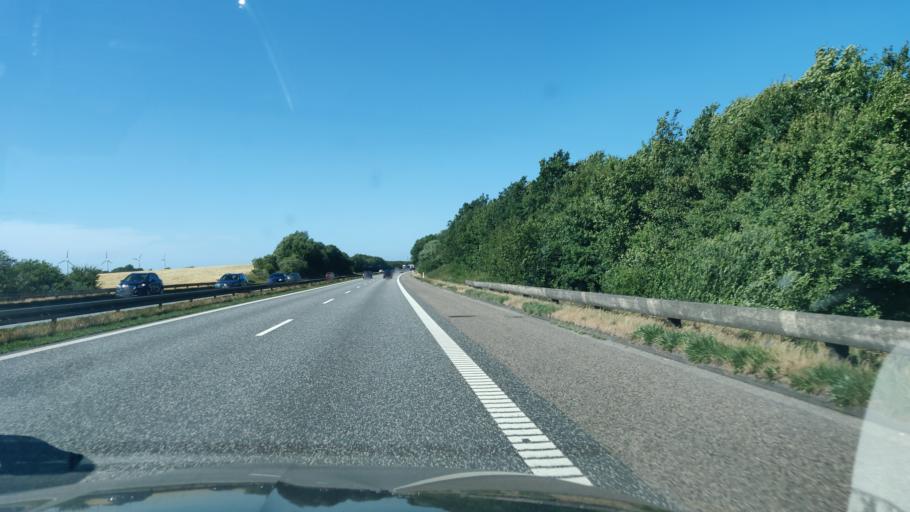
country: DK
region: Central Jutland
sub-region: Favrskov Kommune
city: Hadsten
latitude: 56.3454
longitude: 10.1196
